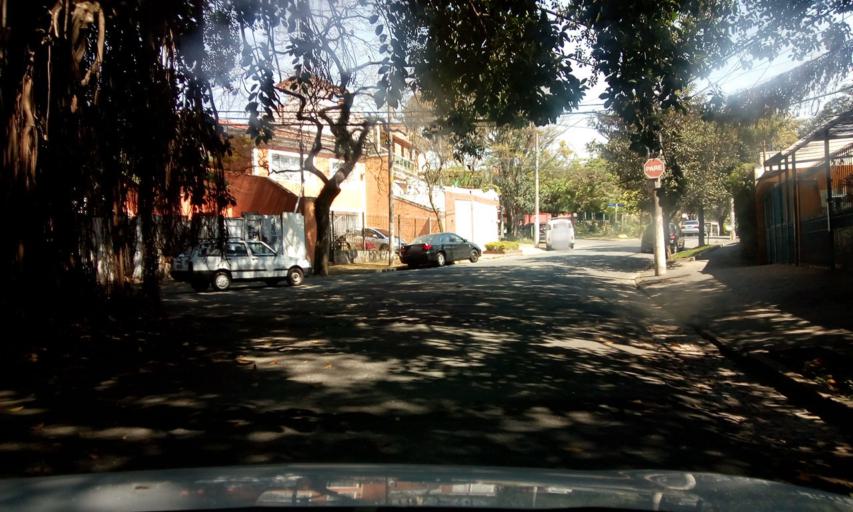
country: BR
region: Sao Paulo
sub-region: Sao Paulo
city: Sao Paulo
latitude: -23.5236
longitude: -46.7114
